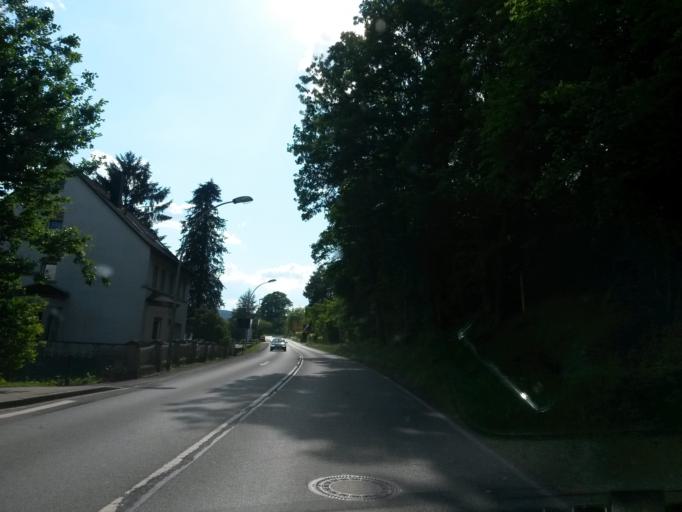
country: DE
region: North Rhine-Westphalia
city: Plettenberg
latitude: 51.1984
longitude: 7.8244
